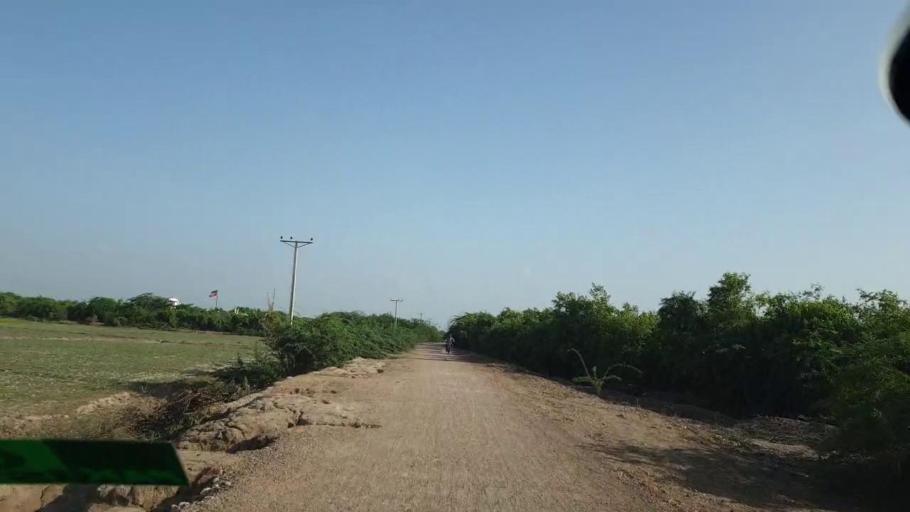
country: PK
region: Sindh
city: Naukot
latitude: 24.7361
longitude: 69.2496
